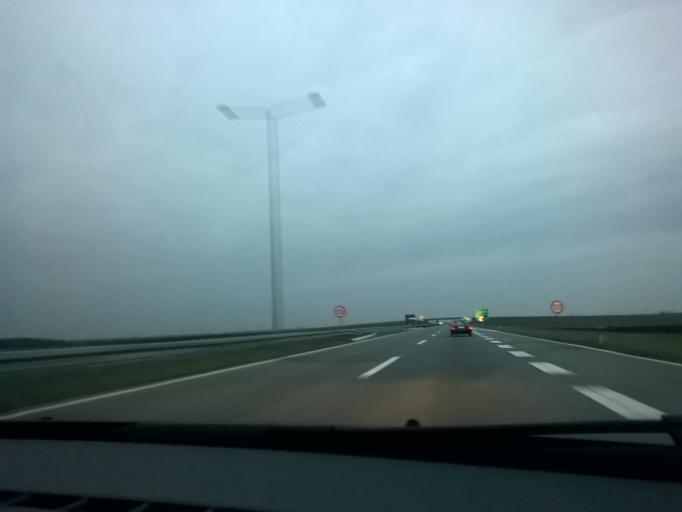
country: RS
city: Krcedin
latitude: 45.0933
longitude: 20.1217
